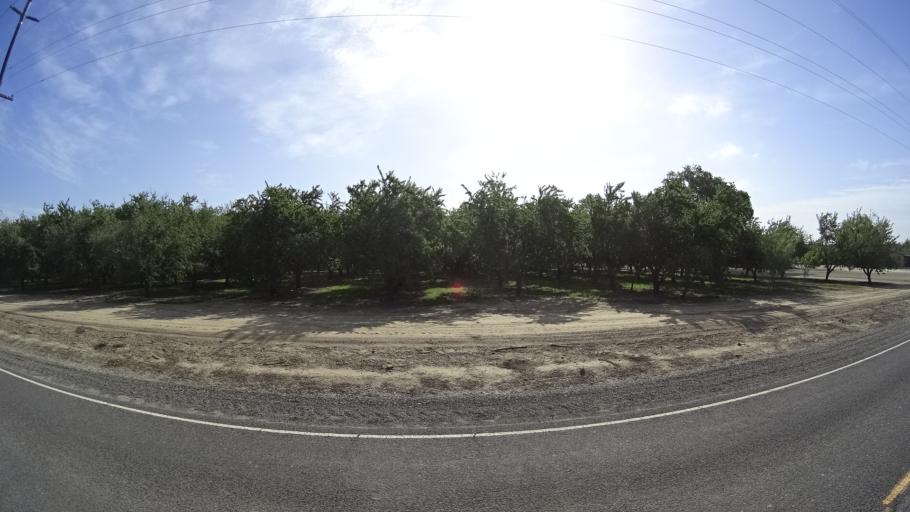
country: US
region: California
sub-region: Glenn County
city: Hamilton City
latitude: 39.6139
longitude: -122.0075
